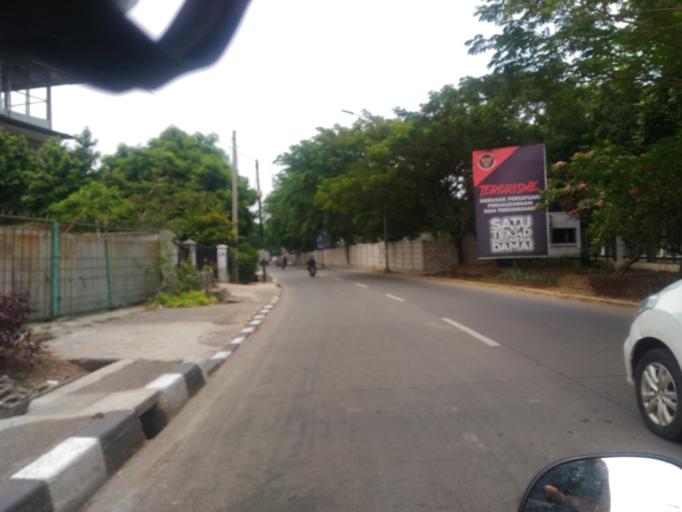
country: ID
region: West Java
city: Depok
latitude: -6.3111
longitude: 106.8382
